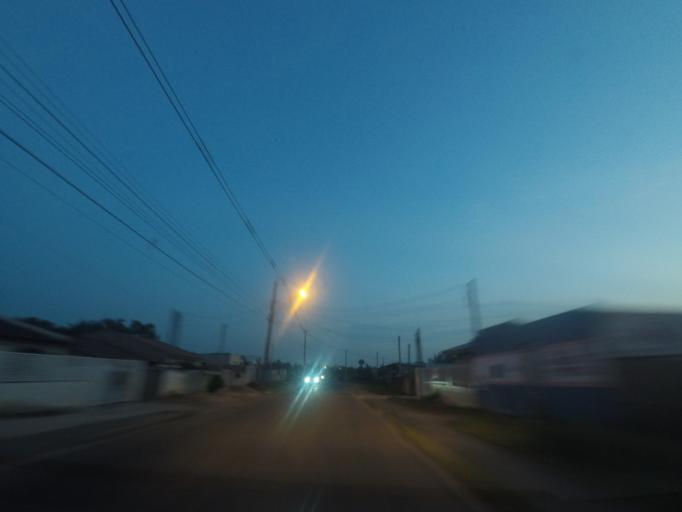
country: BR
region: Parana
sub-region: Pinhais
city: Pinhais
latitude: -25.4705
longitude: -49.1472
